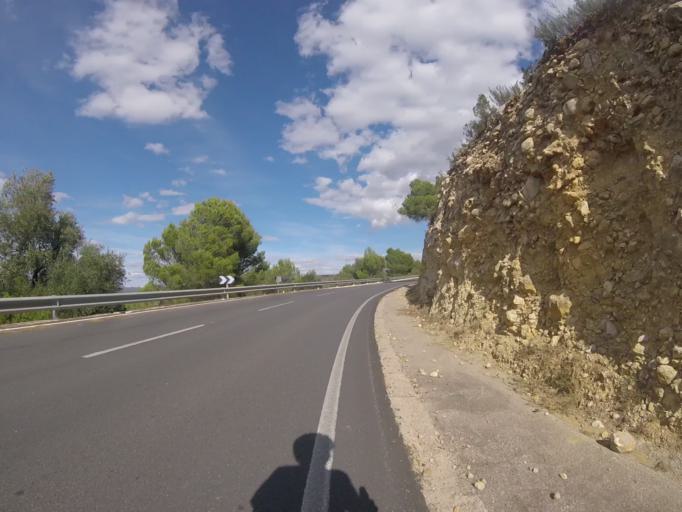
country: ES
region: Valencia
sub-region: Provincia de Castello
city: Cuevas de Vinroma
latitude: 40.3198
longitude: 0.1315
